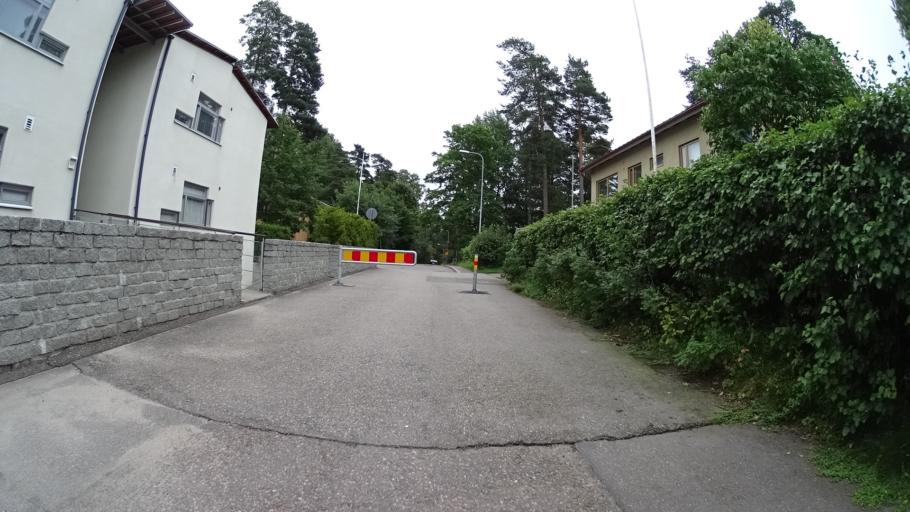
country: FI
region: Uusimaa
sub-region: Helsinki
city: Teekkarikylae
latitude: 60.1989
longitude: 24.8700
